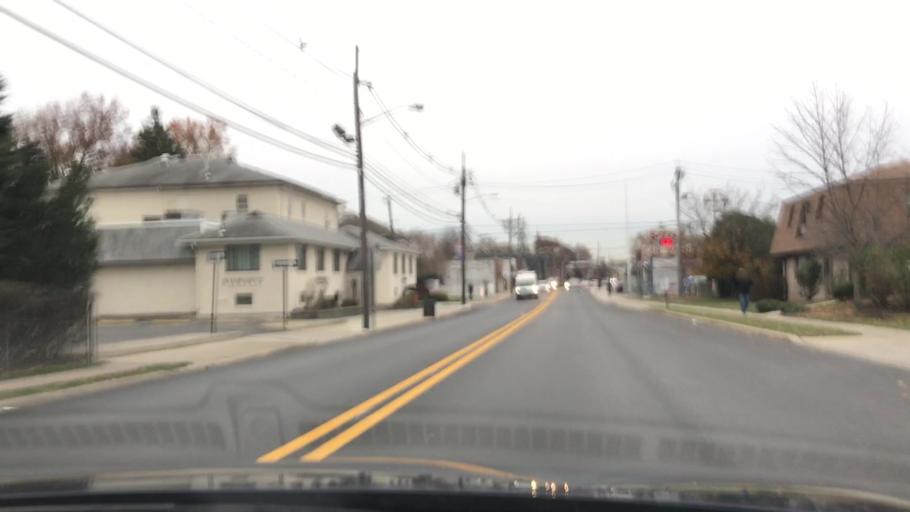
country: US
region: New Jersey
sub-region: Bergen County
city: Bergenfield
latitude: 40.9220
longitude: -73.9969
